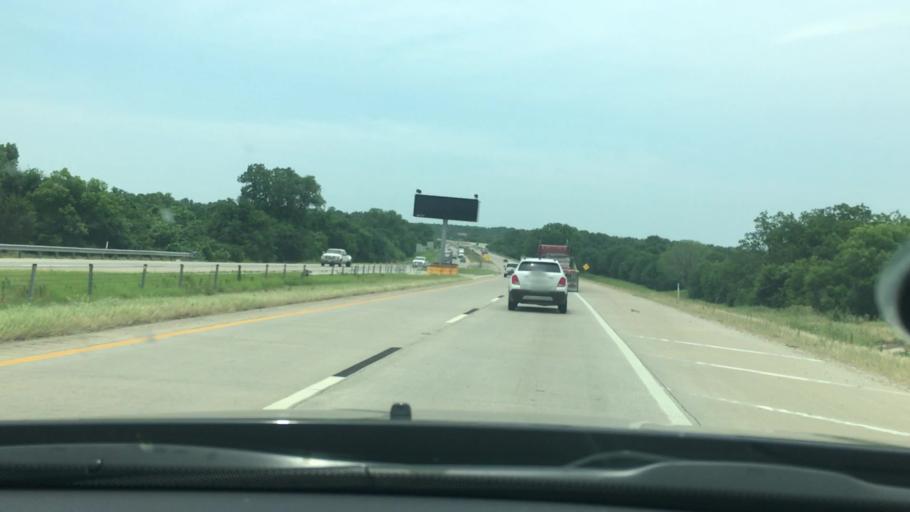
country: US
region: Texas
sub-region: Cooke County
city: Gainesville
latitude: 33.7335
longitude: -97.1532
